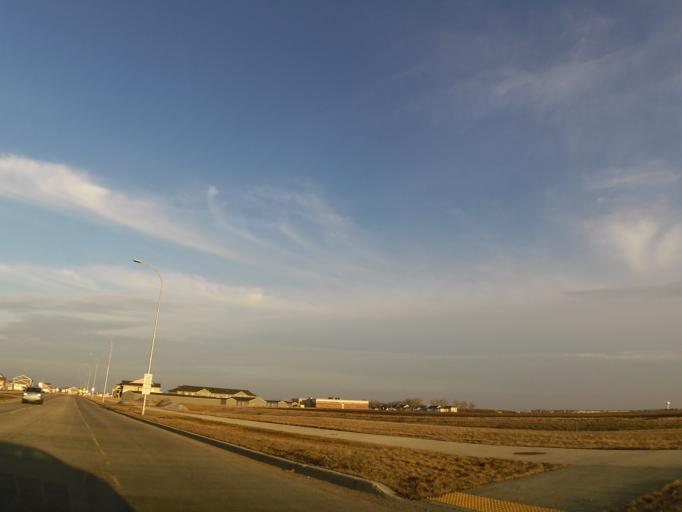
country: US
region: North Dakota
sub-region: Grand Forks County
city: Grand Forks
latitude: 47.8824
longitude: -97.0823
